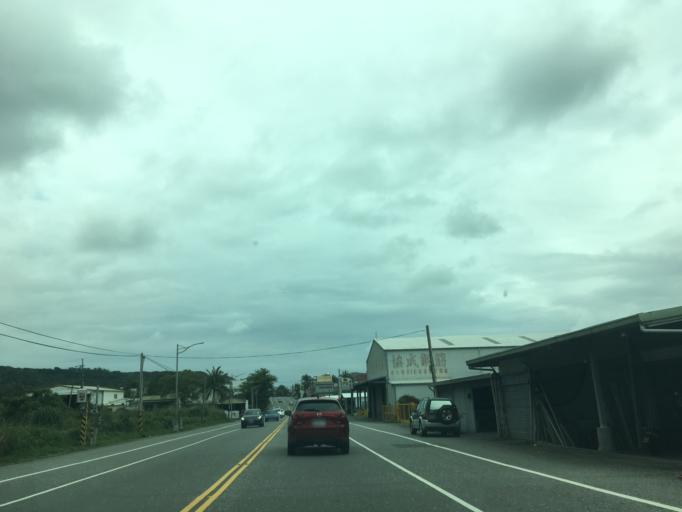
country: TW
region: Taiwan
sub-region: Taitung
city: Taitung
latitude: 23.1084
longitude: 121.3830
